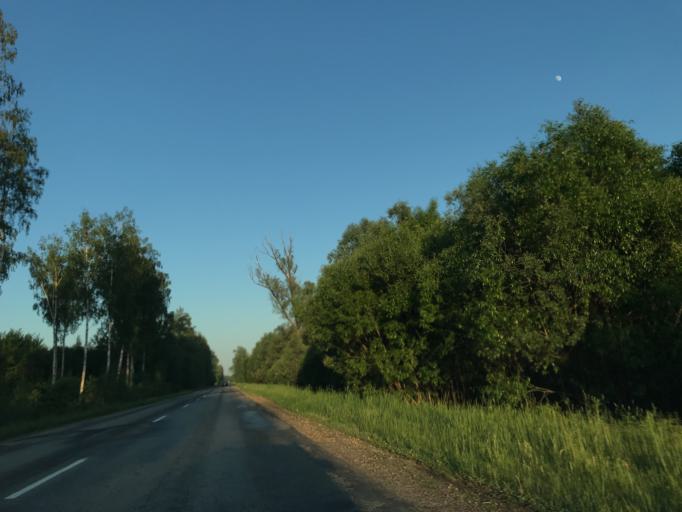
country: LV
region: Vecumnieki
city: Vecumnieki
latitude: 56.5416
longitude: 24.6270
